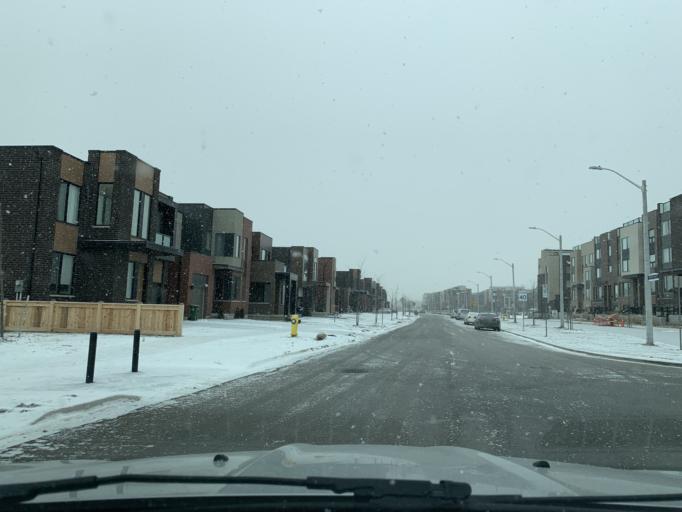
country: CA
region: Ontario
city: Concord
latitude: 43.7325
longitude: -79.4776
